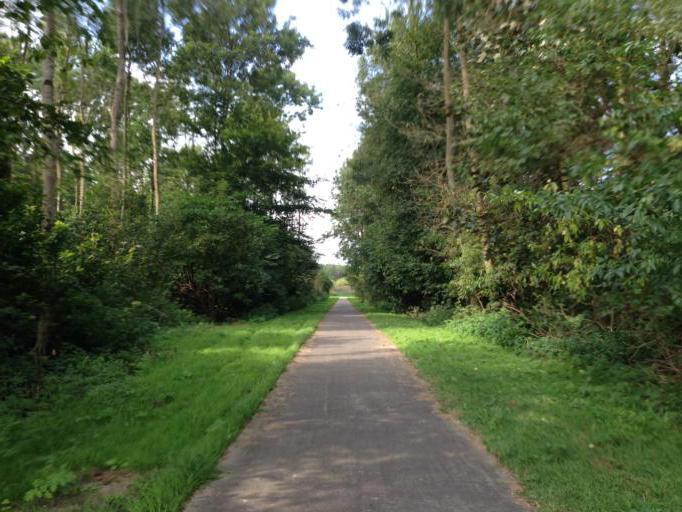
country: NL
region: North Holland
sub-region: Gemeente Huizen
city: Huizen
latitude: 52.3482
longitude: 5.2800
